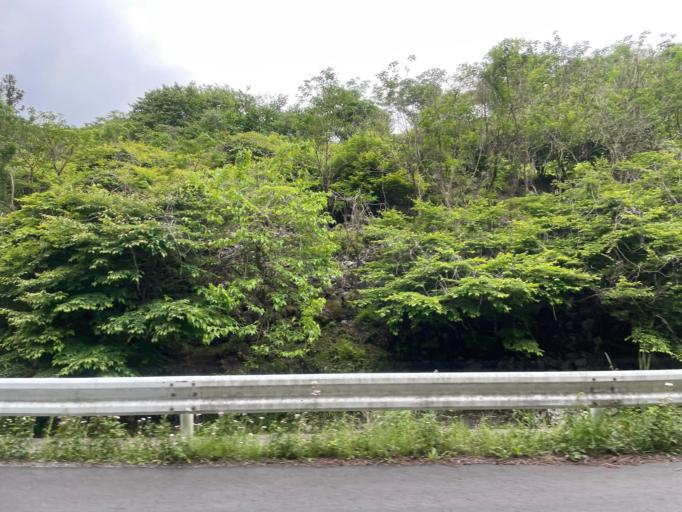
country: JP
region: Tochigi
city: Tanuma
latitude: 36.4625
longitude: 139.6026
